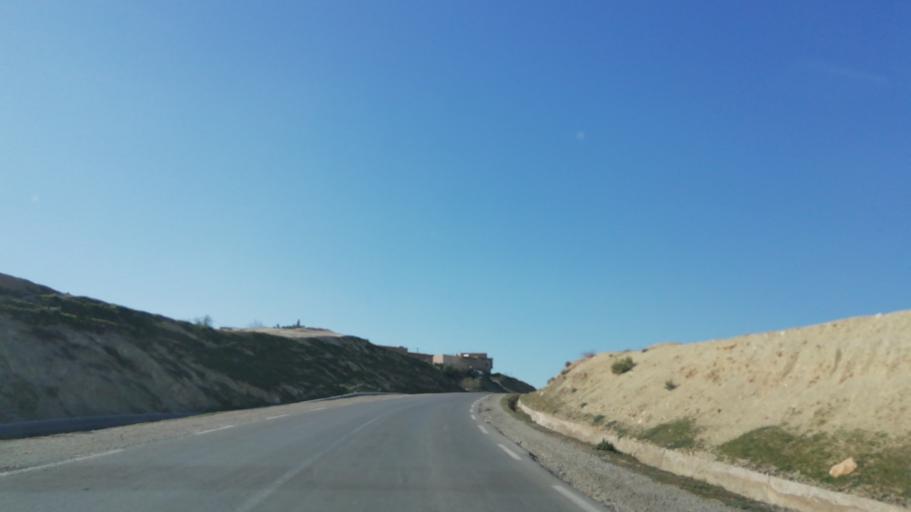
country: DZ
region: Mascara
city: Oued el Abtal
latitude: 35.4553
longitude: 0.7115
